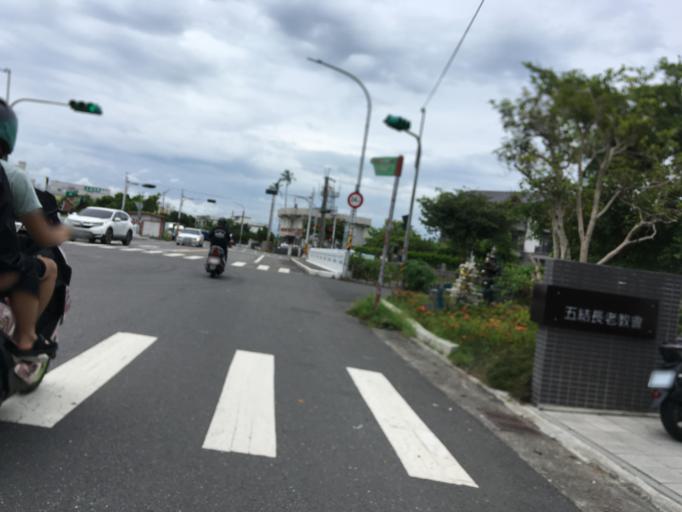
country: TW
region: Taiwan
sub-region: Yilan
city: Yilan
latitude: 24.6866
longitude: 121.7979
